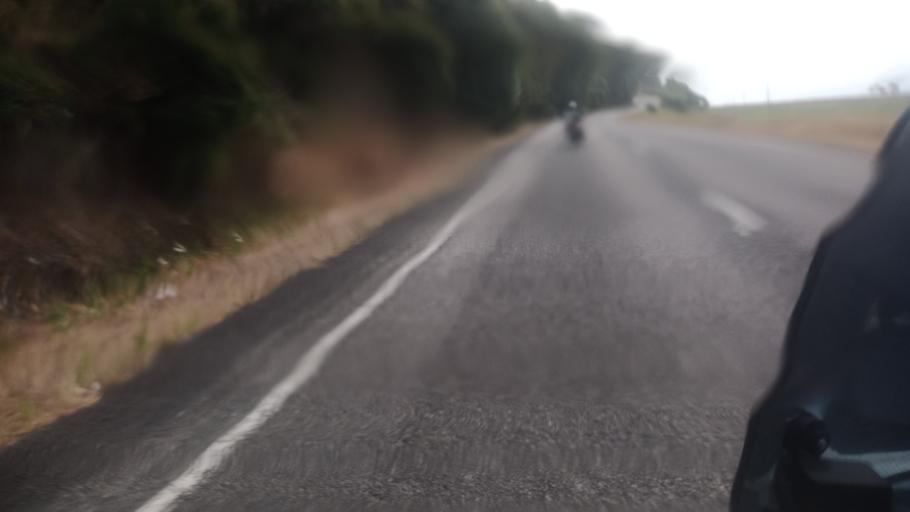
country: NZ
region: Bay of Plenty
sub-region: Opotiki District
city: Opotiki
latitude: -37.8691
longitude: 177.5984
